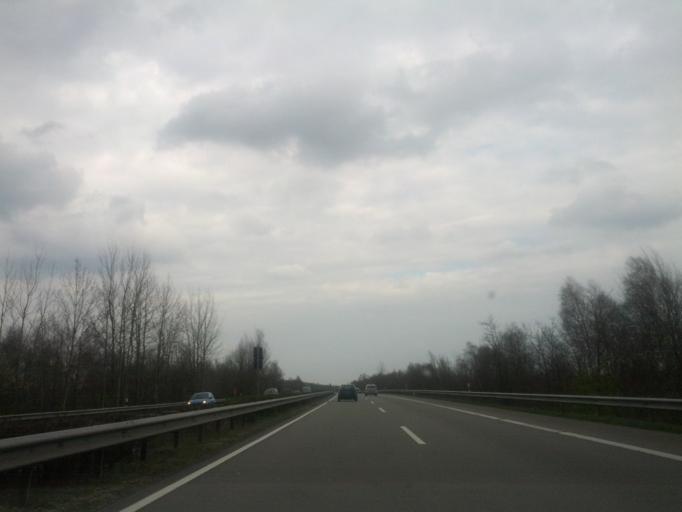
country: DE
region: Lower Saxony
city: Apen
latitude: 53.2806
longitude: 7.8268
